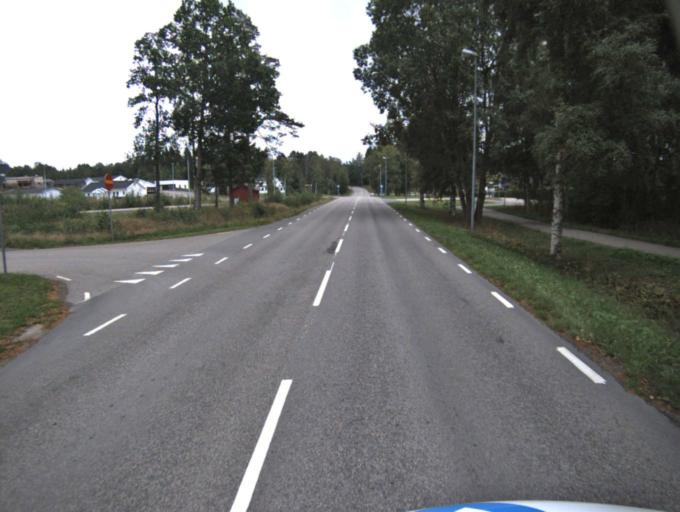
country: SE
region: Vaestra Goetaland
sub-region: Ulricehamns Kommun
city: Ulricehamn
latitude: 57.7798
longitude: 13.4235
